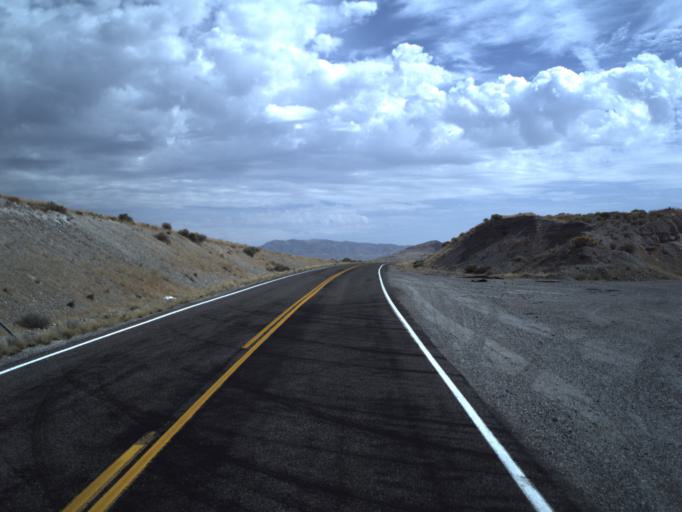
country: US
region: Utah
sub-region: Tooele County
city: Wendover
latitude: 41.4188
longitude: -113.9102
